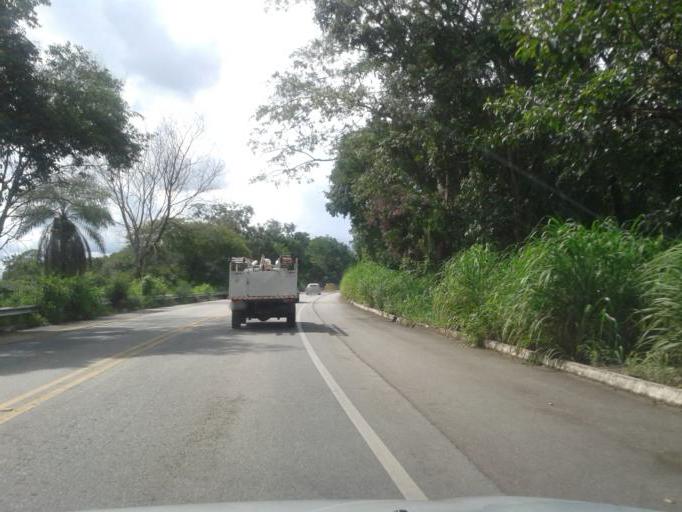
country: BR
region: Goias
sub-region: Goias
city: Goias
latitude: -15.8294
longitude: -50.1164
